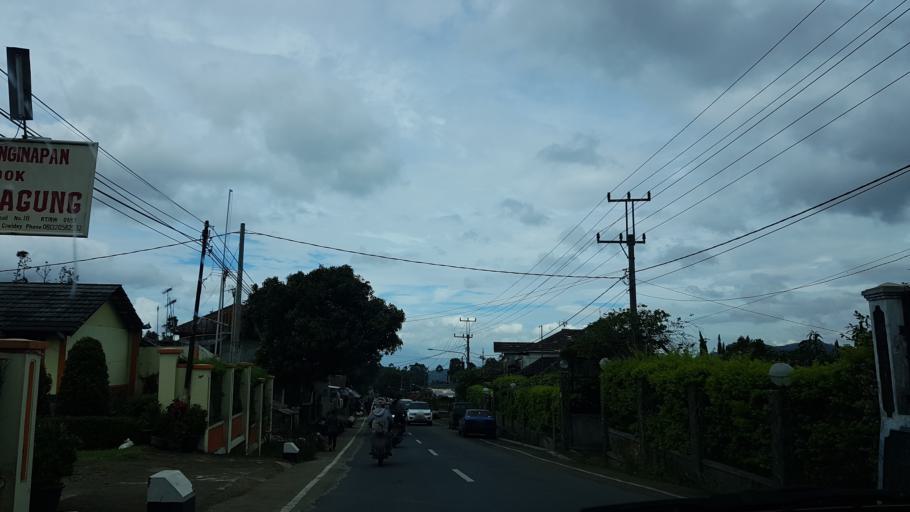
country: ID
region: West Java
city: Banjar
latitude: -7.1135
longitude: 107.4393
